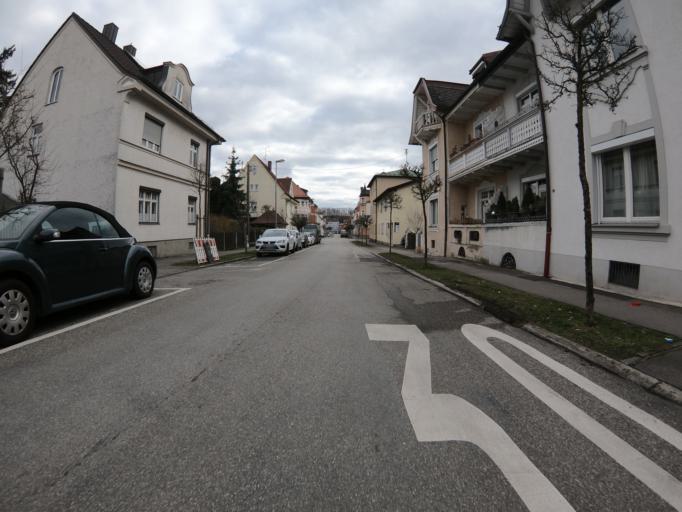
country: DE
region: Bavaria
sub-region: Upper Bavaria
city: Fuerstenfeldbruck
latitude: 48.1781
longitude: 11.2493
